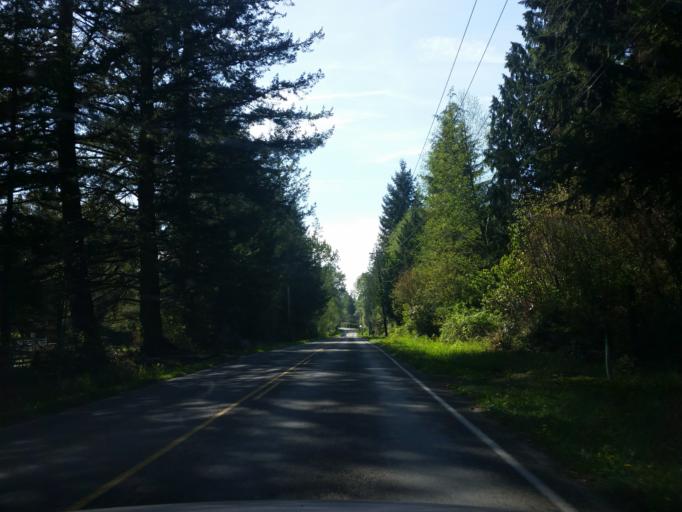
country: US
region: Washington
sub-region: Snohomish County
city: Machias
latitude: 47.9634
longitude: -122.0347
